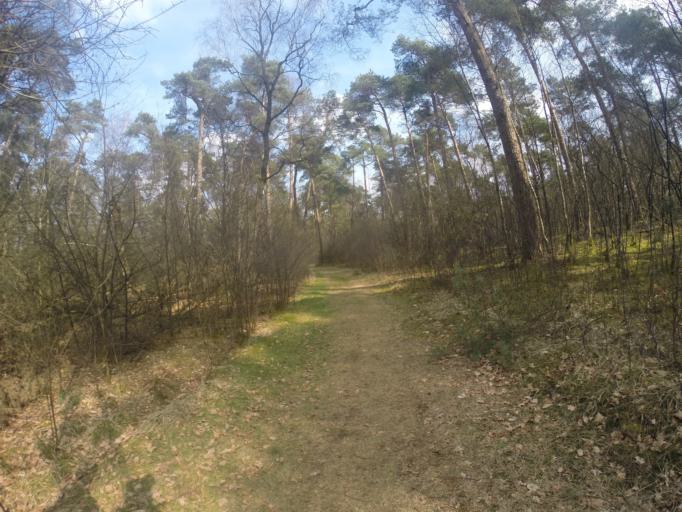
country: NL
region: Gelderland
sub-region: Gemeente Lochem
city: Almen
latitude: 52.1496
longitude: 6.3267
